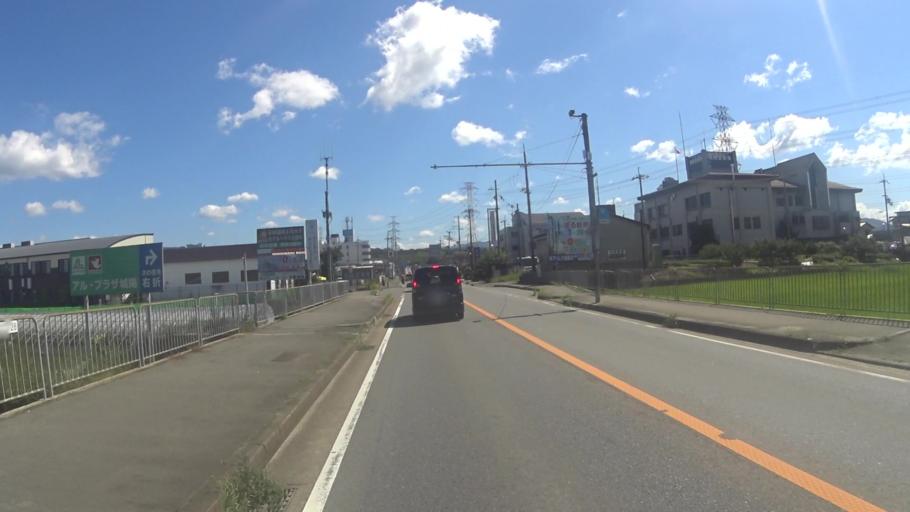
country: JP
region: Kyoto
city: Tanabe
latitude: 34.8469
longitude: 135.7782
